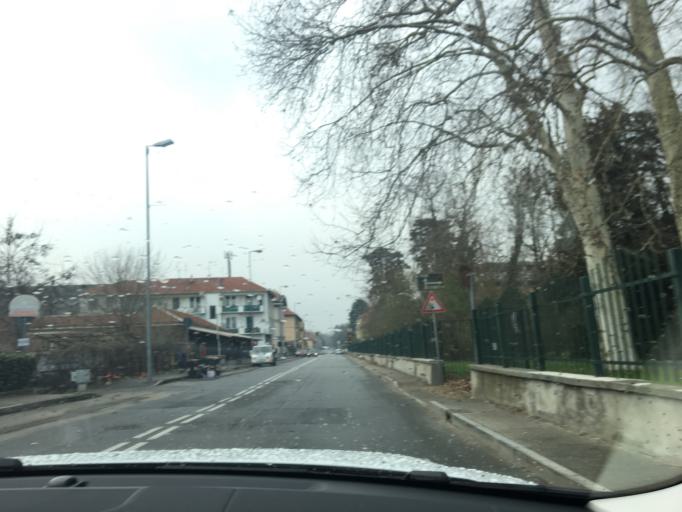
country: IT
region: Piedmont
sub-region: Provincia di Torino
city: Moncalieri
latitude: 45.0180
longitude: 7.6796
